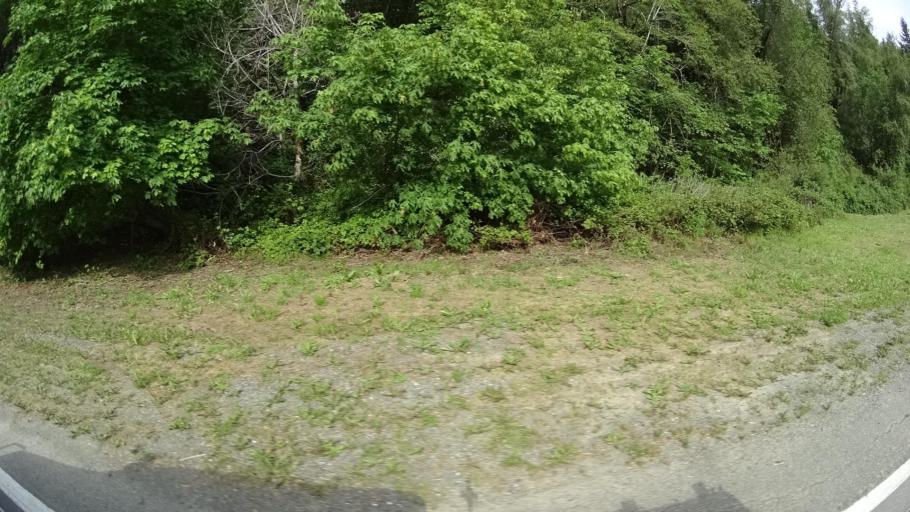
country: US
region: California
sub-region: Humboldt County
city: Redway
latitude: 40.2212
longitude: -123.8082
